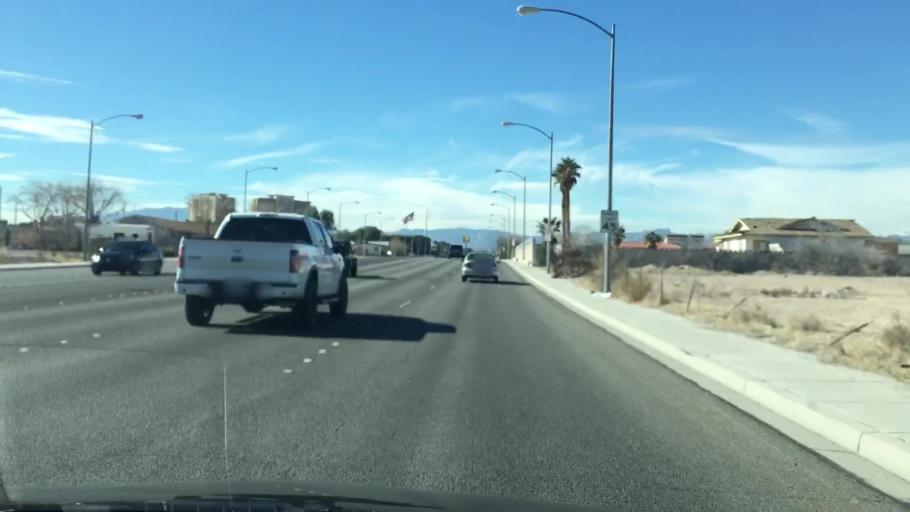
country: US
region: Nevada
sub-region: Clark County
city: Paradise
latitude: 36.0424
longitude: -115.1638
